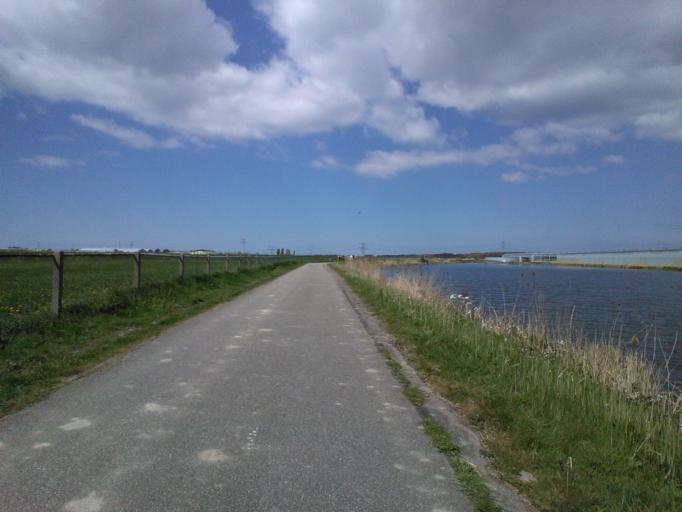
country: NL
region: South Holland
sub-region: Gemeente Westland
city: Maasdijk
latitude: 51.9543
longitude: 4.1933
